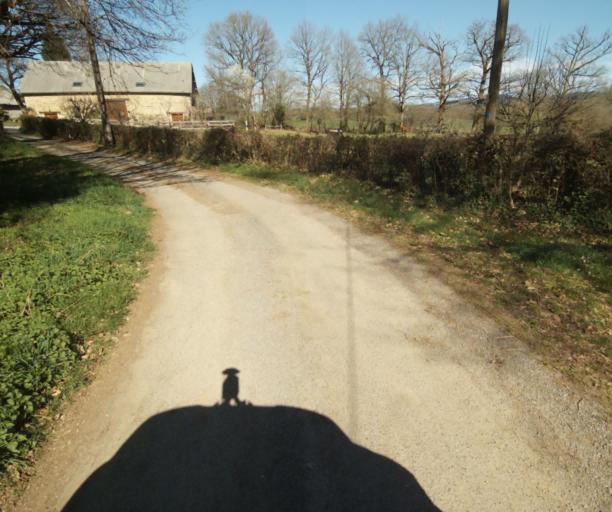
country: FR
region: Limousin
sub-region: Departement de la Correze
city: Chamboulive
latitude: 45.4644
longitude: 1.7471
